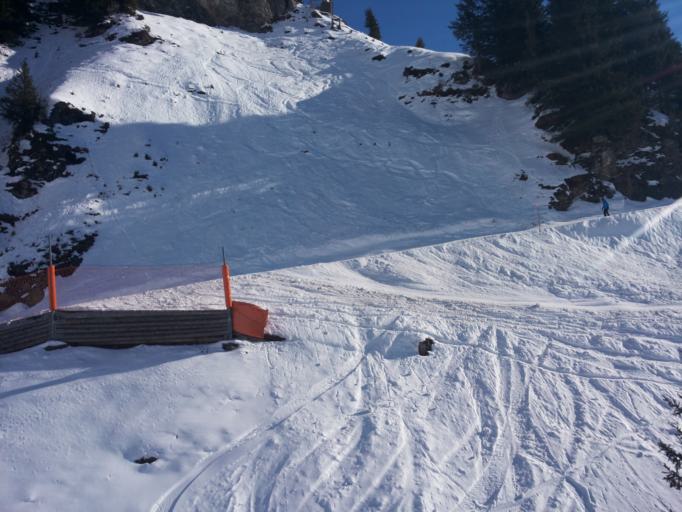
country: CH
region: Bern
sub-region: Interlaken-Oberhasli District
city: Meiringen
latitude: 46.7491
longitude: 8.2378
